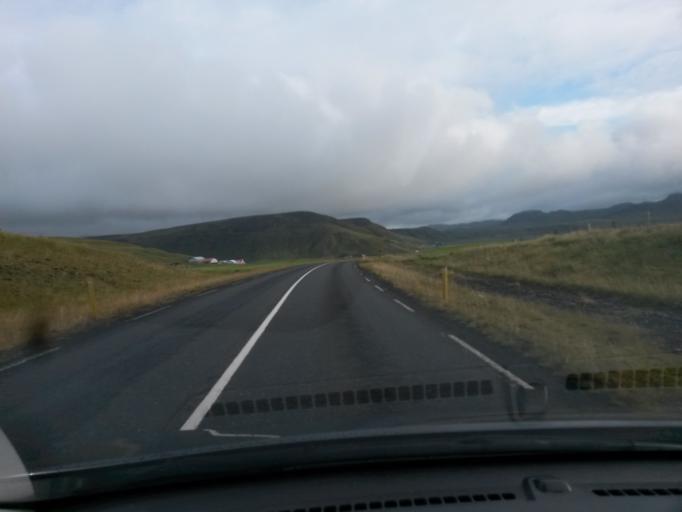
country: IS
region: South
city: Vestmannaeyjar
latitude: 63.4377
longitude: -19.1571
